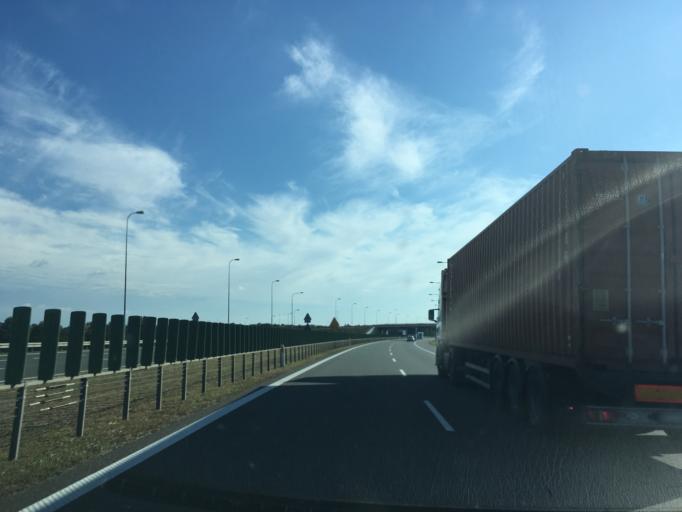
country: PL
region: Kujawsko-Pomorskie
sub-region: Grudziadz
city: Grudziadz
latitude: 53.4309
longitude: 18.6925
